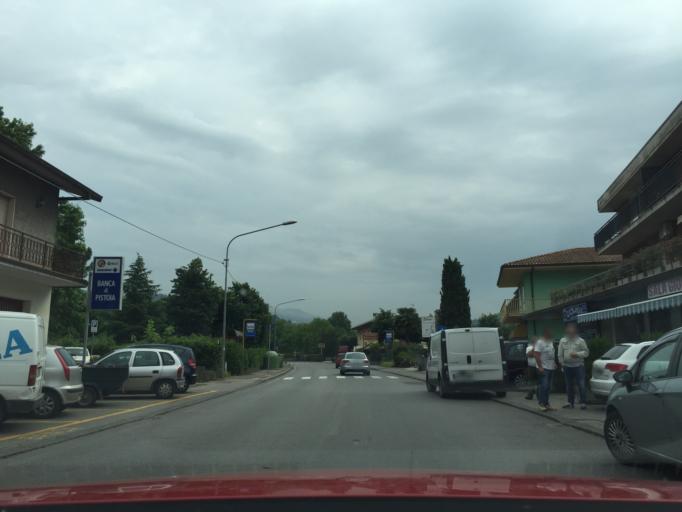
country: IT
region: Tuscany
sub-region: Provincia di Pistoia
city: Pieve a Nievole
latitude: 43.8834
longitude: 10.8090
